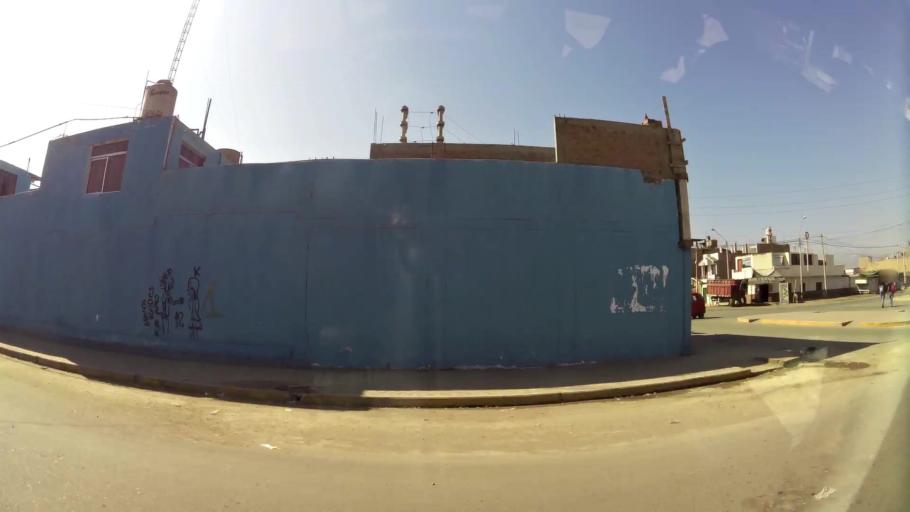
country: PE
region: Ica
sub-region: Provincia de Chincha
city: Chincha Alta
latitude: -13.4102
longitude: -76.1284
